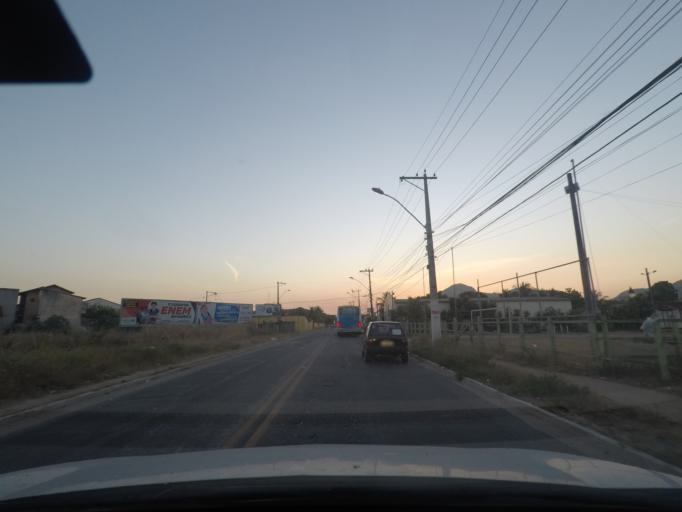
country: BR
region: Rio de Janeiro
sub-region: Niteroi
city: Niteroi
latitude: -22.9607
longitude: -42.9851
